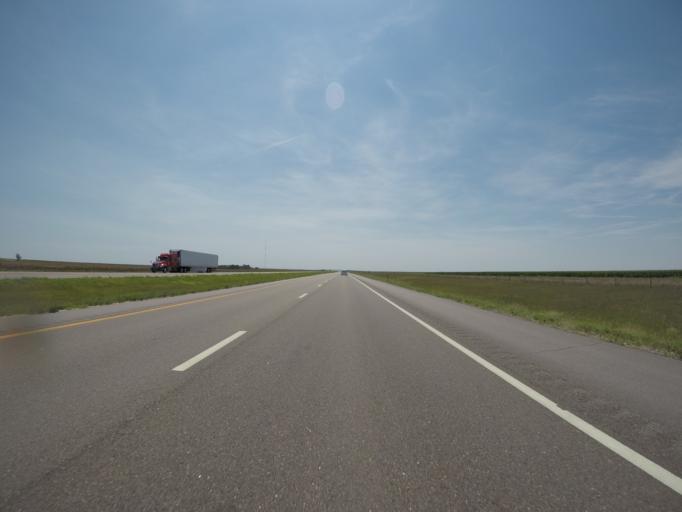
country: US
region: Kansas
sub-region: Logan County
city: Oakley
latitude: 39.2490
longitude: -100.9179
